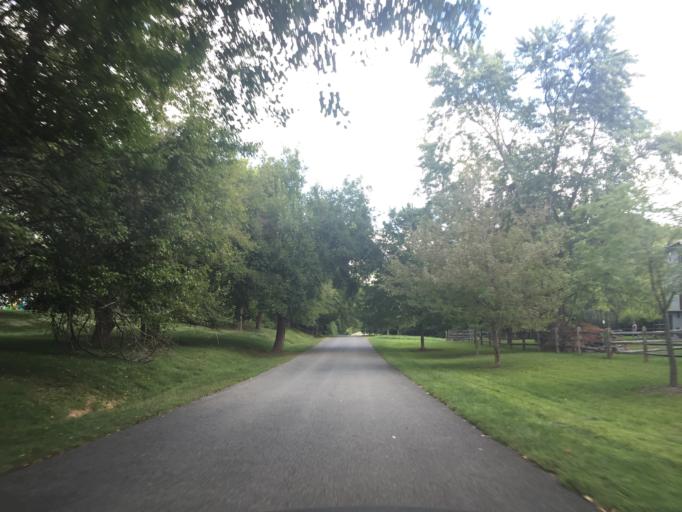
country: US
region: Maryland
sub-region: Montgomery County
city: Montgomery Village
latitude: 39.1650
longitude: -77.1770
